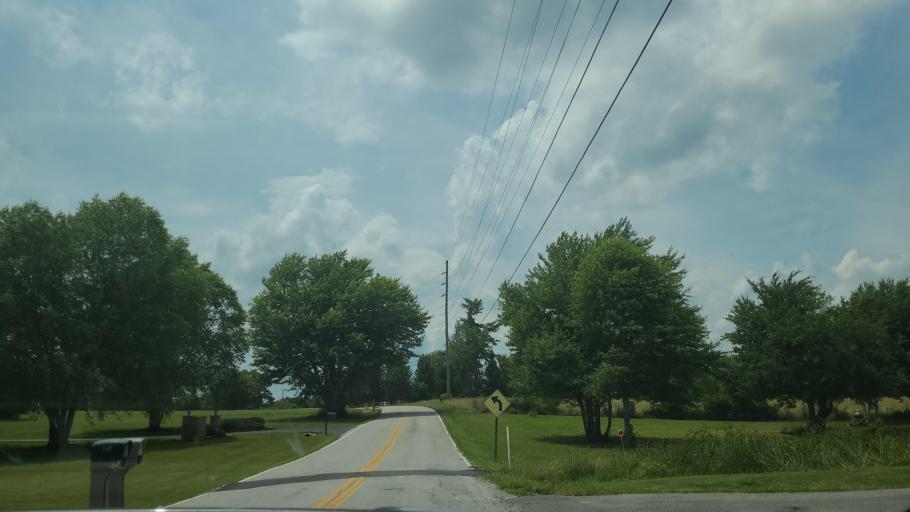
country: US
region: Tennessee
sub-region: Cumberland County
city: Crossville
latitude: 35.9083
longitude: -85.0133
